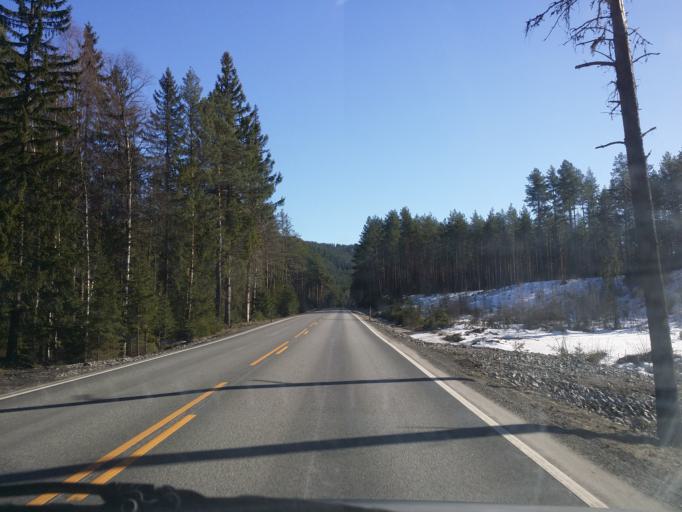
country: NO
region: Buskerud
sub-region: Ringerike
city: Honefoss
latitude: 60.2881
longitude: 10.1891
